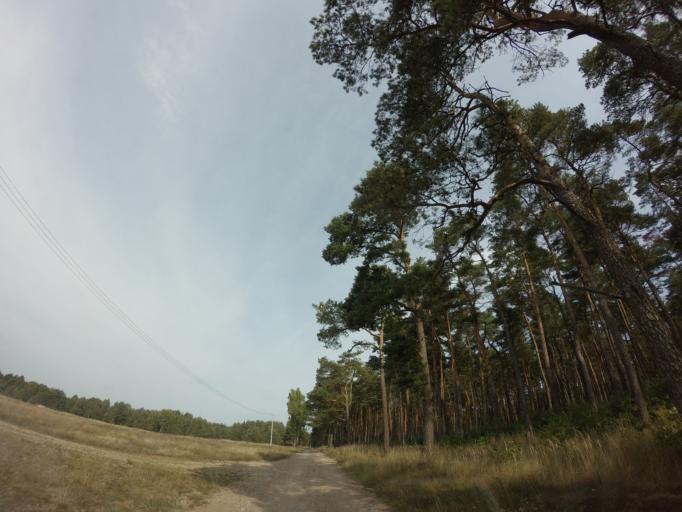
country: PL
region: West Pomeranian Voivodeship
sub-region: Powiat drawski
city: Drawsko Pomorskie
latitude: 53.4678
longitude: 15.7138
